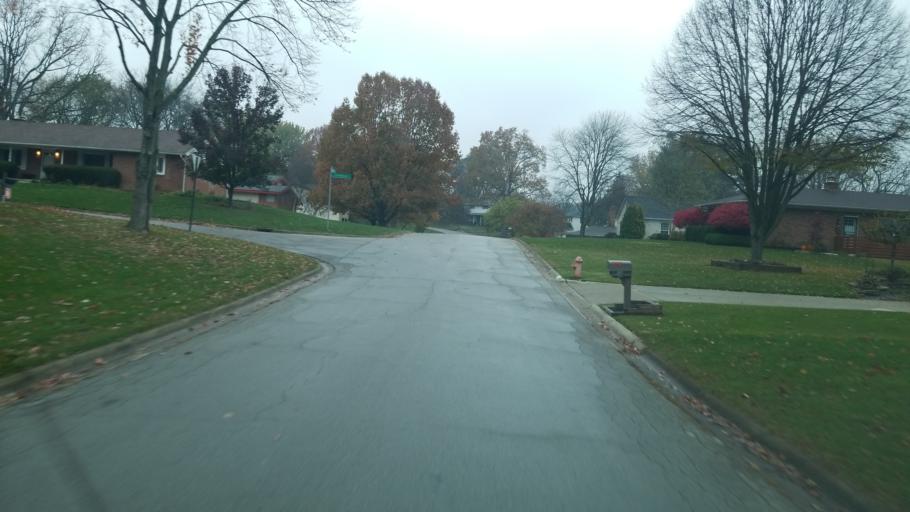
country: US
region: Ohio
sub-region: Franklin County
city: Worthington
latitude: 40.0805
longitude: -83.0403
